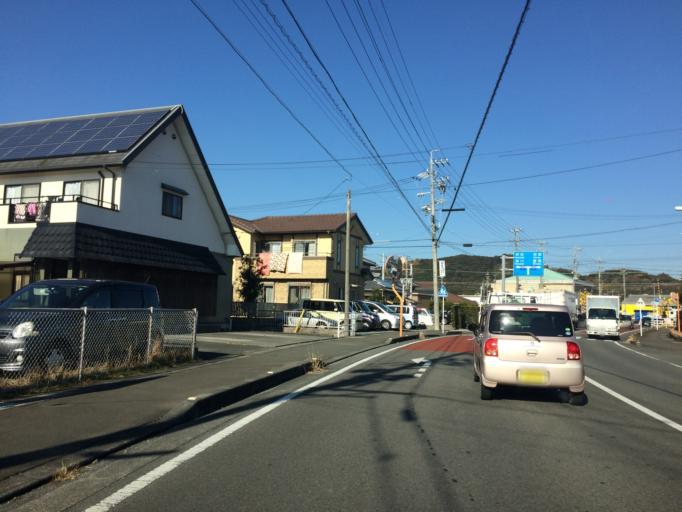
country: JP
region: Shizuoka
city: Shimada
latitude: 34.8372
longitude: 138.2102
